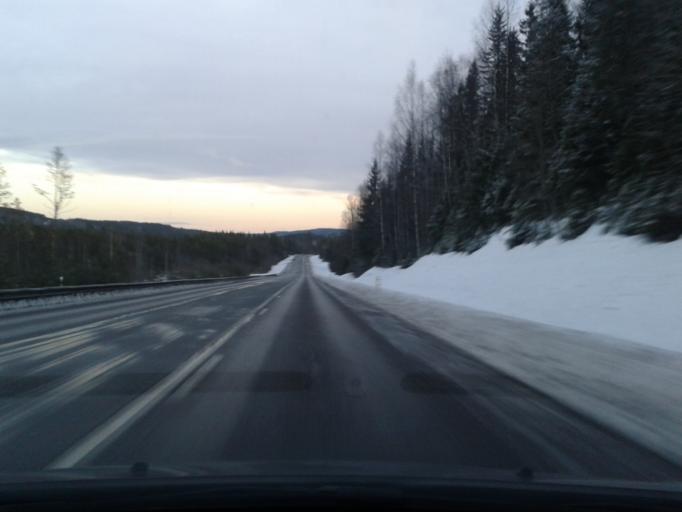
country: SE
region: Vaesternorrland
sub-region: Kramfors Kommun
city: Bollstabruk
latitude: 63.1101
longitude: 17.5026
